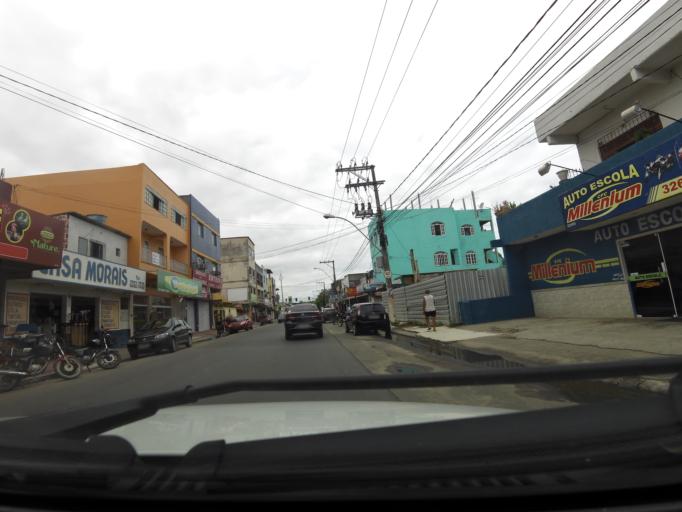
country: BR
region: Espirito Santo
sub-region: Guarapari
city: Guarapari
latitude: -20.6012
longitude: -40.4630
